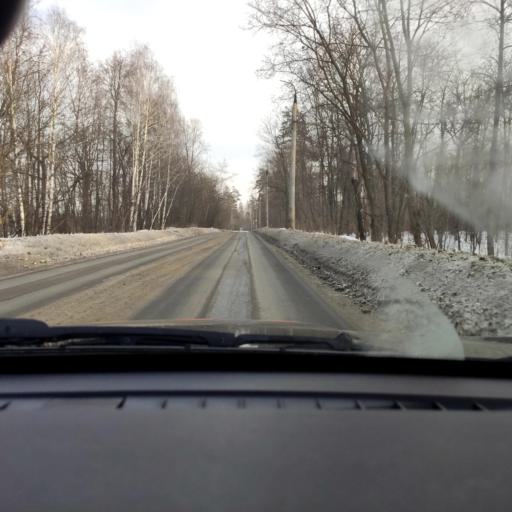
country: RU
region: Samara
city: Pribrezhnyy
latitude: 53.5158
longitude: 49.8469
